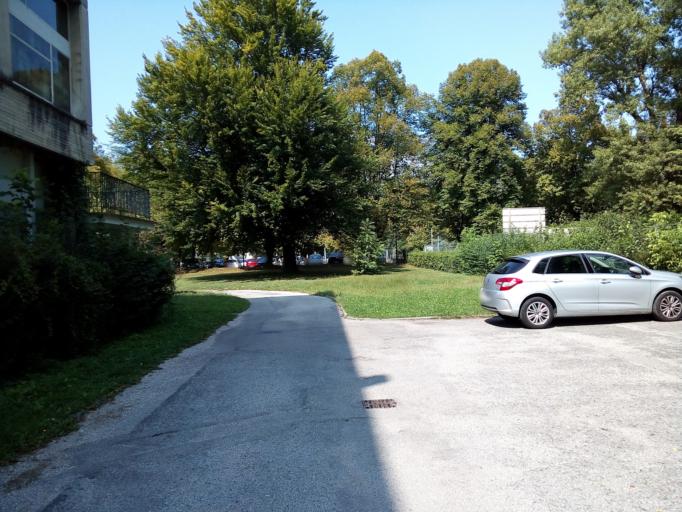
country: FR
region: Rhone-Alpes
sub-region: Departement de l'Isere
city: Corenc
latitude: 45.1933
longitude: 5.7725
